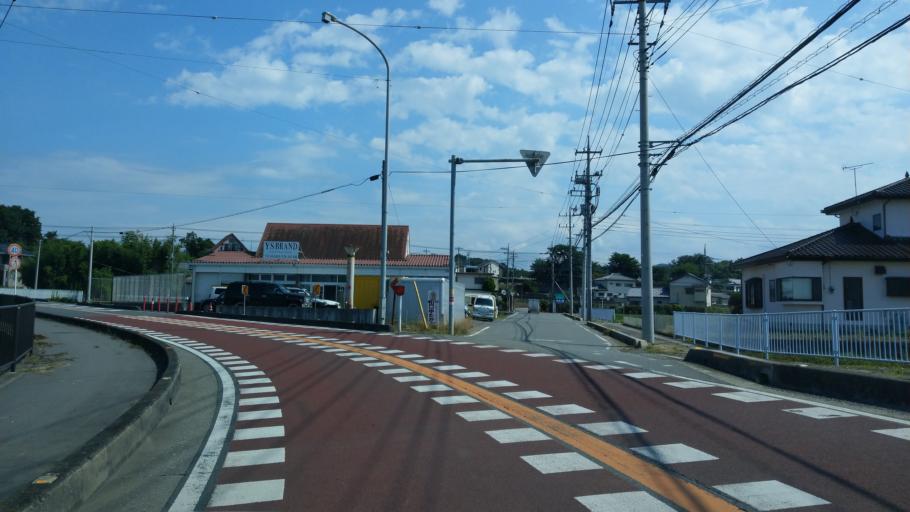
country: JP
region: Saitama
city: Kodamacho-kodamaminami
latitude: 36.2056
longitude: 139.1518
